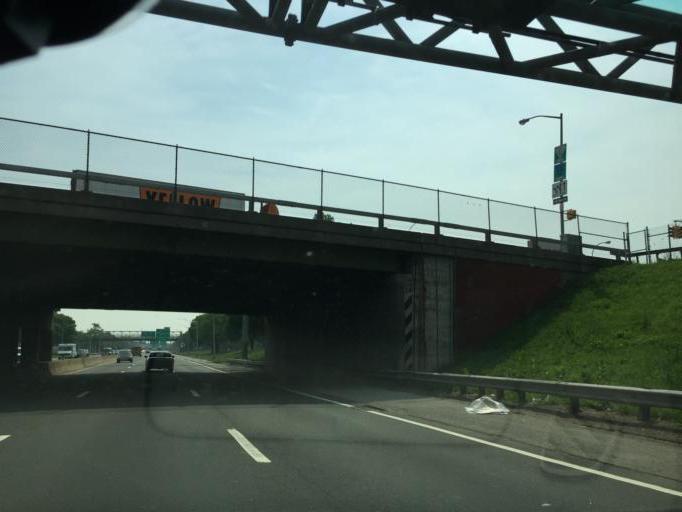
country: US
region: New York
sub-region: Bronx
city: The Bronx
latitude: 40.8259
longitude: -73.8599
